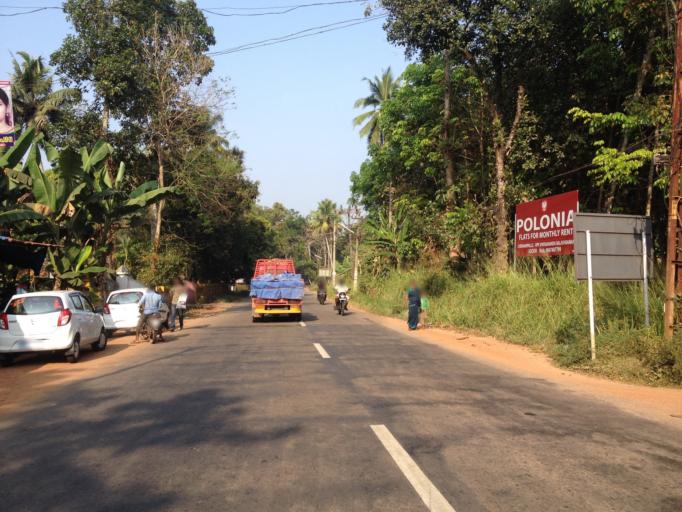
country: IN
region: Kerala
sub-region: Pattanamtitta
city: Adur
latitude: 9.1610
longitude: 76.7144
